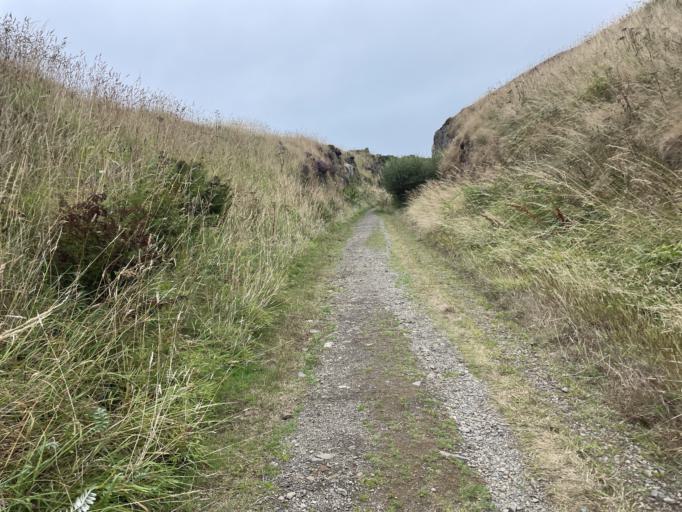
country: GB
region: Scotland
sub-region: Dumfries and Galloway
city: Stranraer
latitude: 54.8368
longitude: -5.1112
